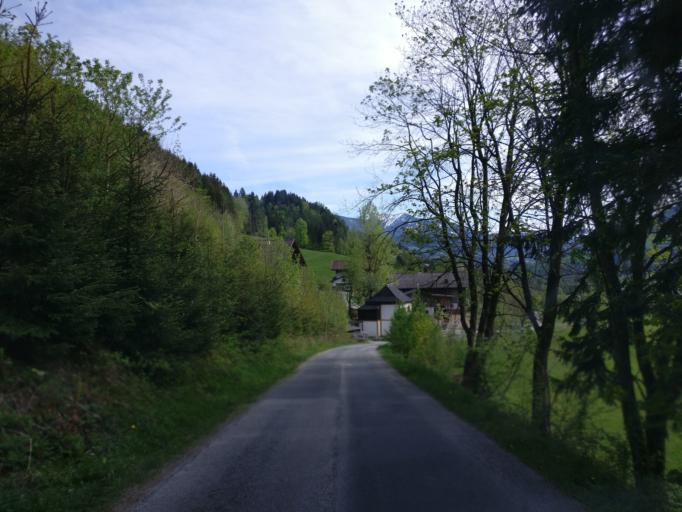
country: AT
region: Salzburg
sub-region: Politischer Bezirk Sankt Johann im Pongau
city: Pfarrwerfen
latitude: 47.4725
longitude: 13.1994
